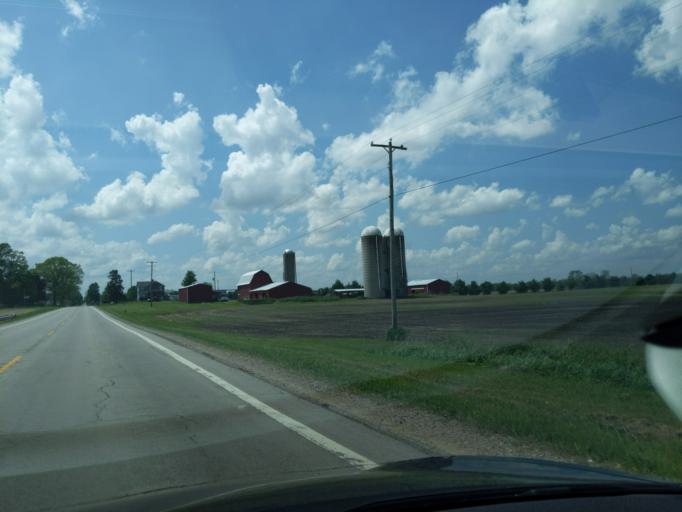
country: US
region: Michigan
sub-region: Ingham County
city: Williamston
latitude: 42.5559
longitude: -84.2837
